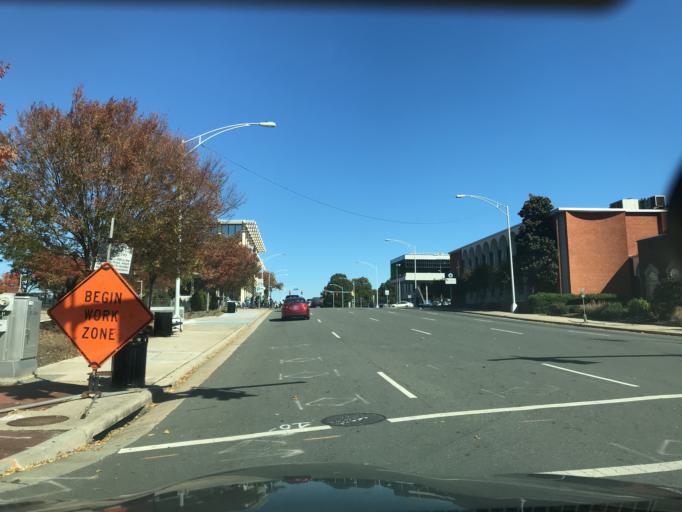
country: US
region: North Carolina
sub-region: Durham County
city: Durham
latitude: 35.9938
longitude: -78.8985
